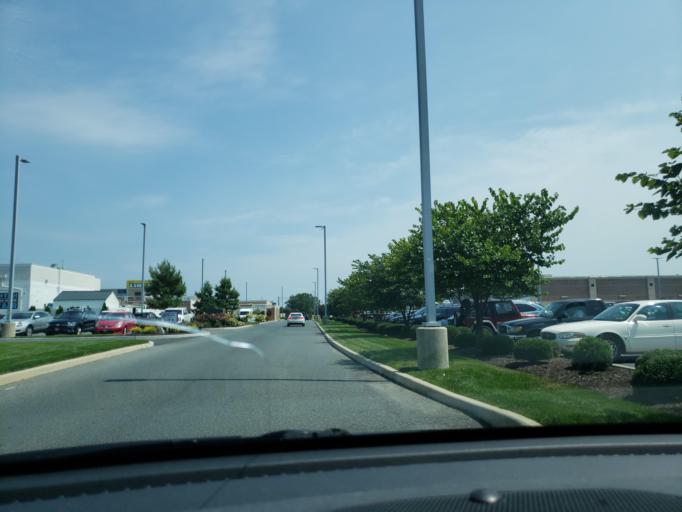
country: US
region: Delaware
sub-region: Sussex County
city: Rehoboth Beach
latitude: 38.7133
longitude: -75.1064
